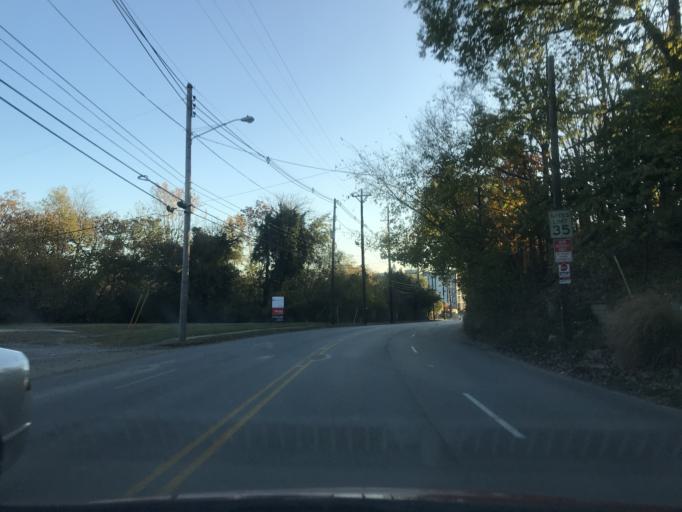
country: US
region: Indiana
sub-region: Clark County
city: Jeffersonville
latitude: 38.2507
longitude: -85.7260
